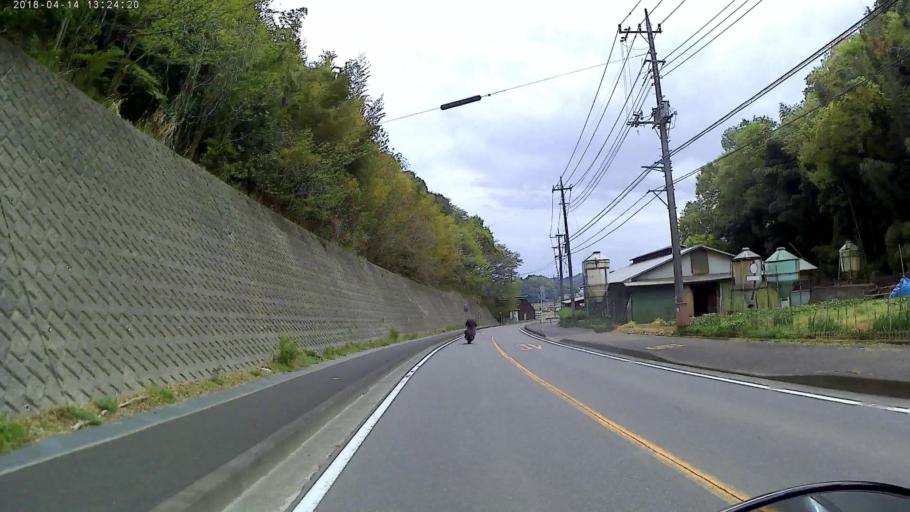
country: JP
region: Kanagawa
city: Hadano
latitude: 35.3336
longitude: 139.2200
